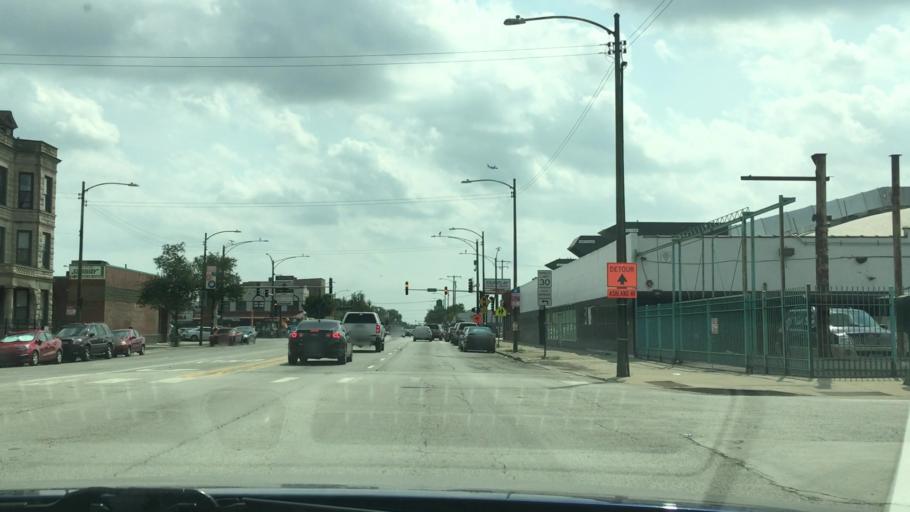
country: US
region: Illinois
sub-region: Cook County
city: Chicago
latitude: 41.8530
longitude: -87.6858
